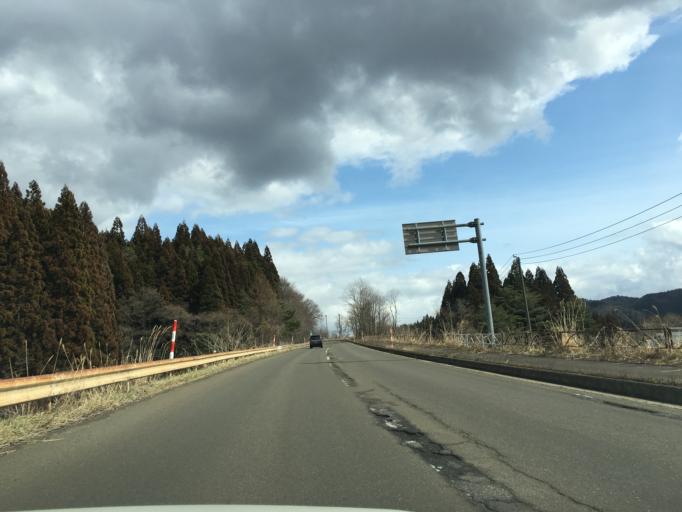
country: JP
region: Akita
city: Odate
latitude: 40.2169
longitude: 140.6303
